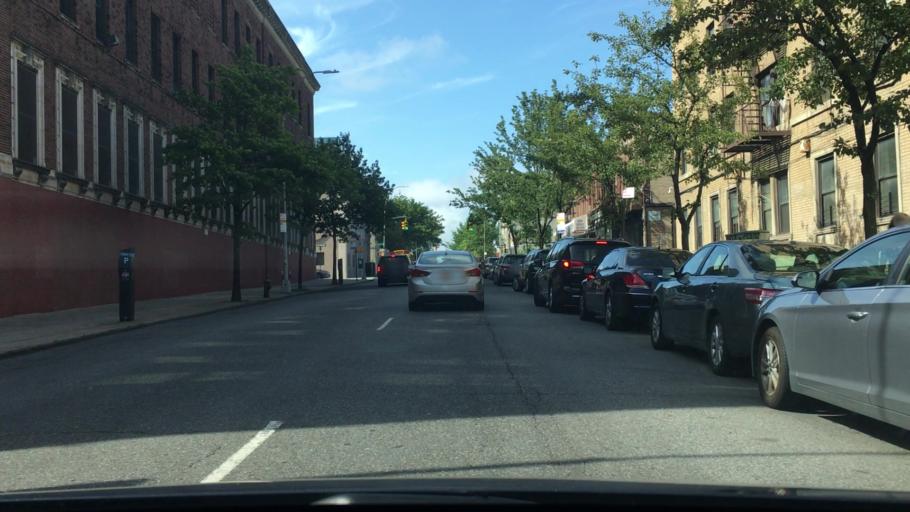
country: US
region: New York
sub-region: Kings County
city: Brooklyn
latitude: 40.6656
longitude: -73.9370
